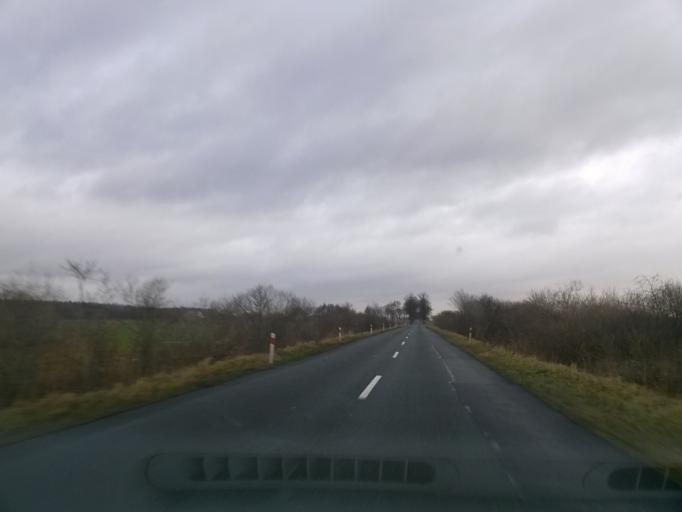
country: PL
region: Kujawsko-Pomorskie
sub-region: Powiat nakielski
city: Kcynia
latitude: 52.9633
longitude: 17.4343
